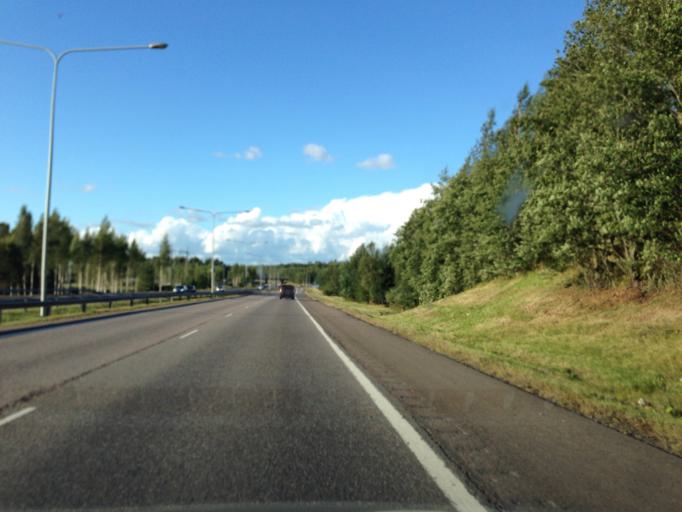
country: FI
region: Uusimaa
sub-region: Helsinki
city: Vantaa
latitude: 60.3347
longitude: 24.9997
